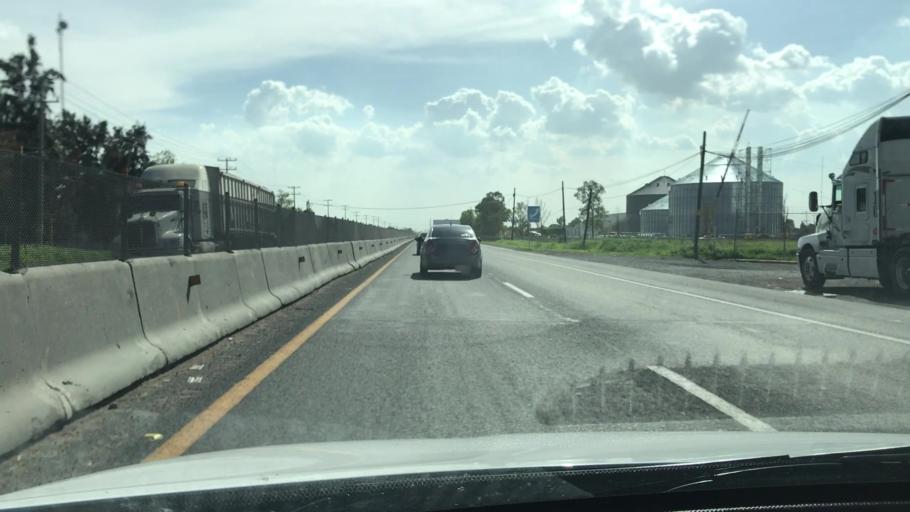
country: MX
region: Guanajuato
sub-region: Cortazar
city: Colonia la Calzada (La Olla)
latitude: 20.5099
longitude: -100.9717
